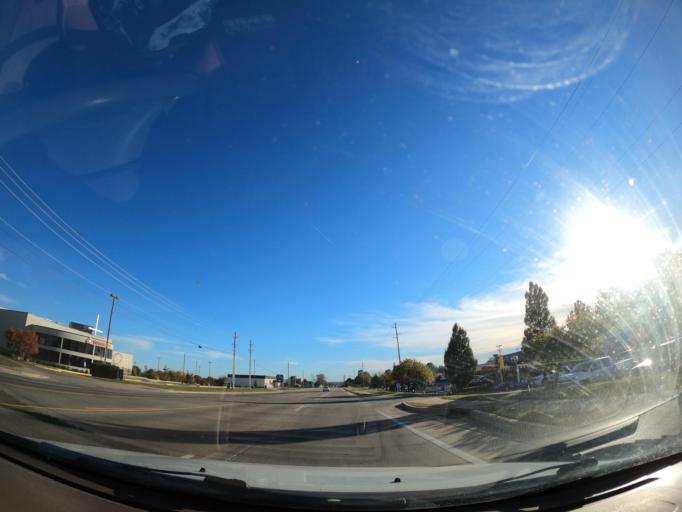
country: US
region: Oklahoma
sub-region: Tulsa County
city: Owasso
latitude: 36.2917
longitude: -95.8302
